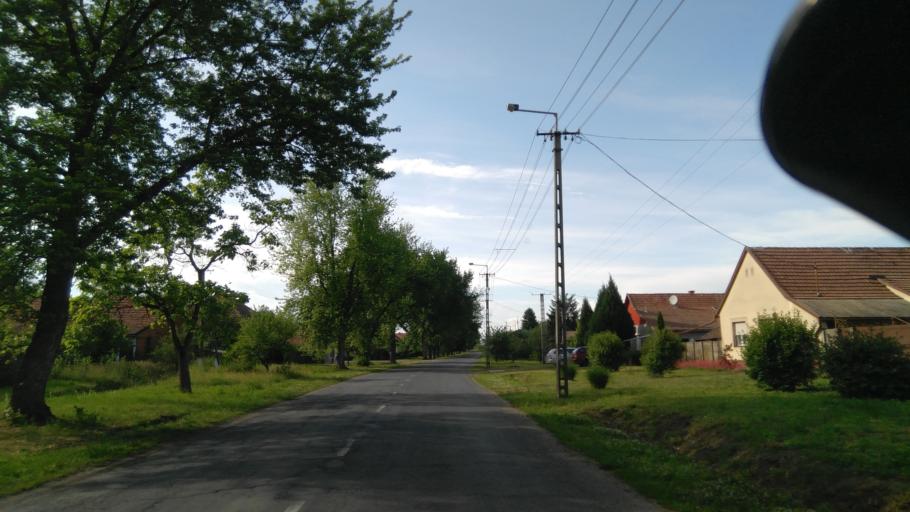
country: HU
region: Bekes
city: Lokoshaza
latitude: 46.4287
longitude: 21.2303
